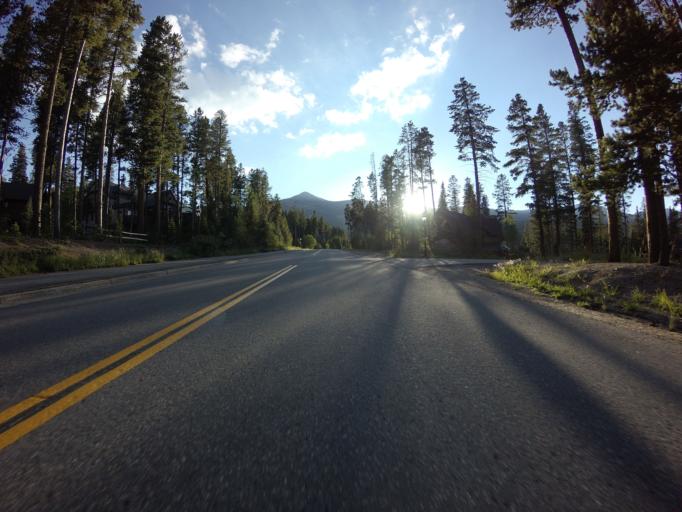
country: US
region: Colorado
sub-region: Summit County
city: Breckenridge
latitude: 39.4817
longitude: -106.0606
